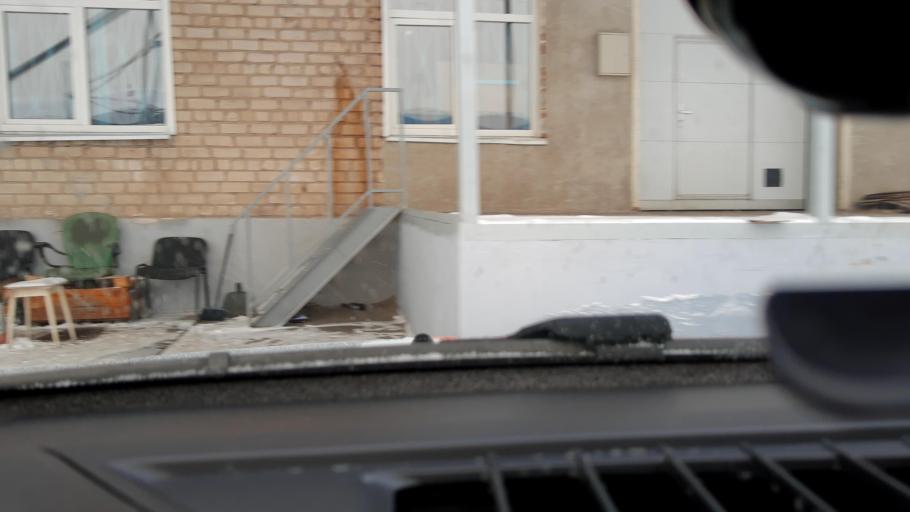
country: RU
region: Nizjnij Novgorod
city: Gorbatovka
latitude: 56.3379
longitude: 43.8119
